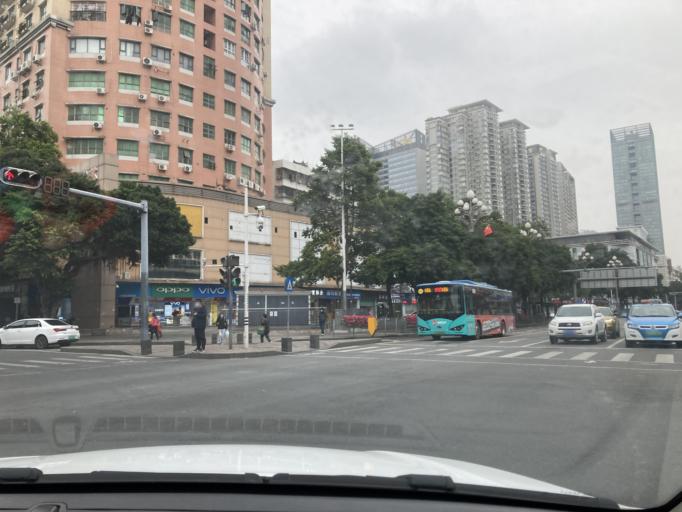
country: CN
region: Guangdong
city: Nantou
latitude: 22.5355
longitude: 113.9142
